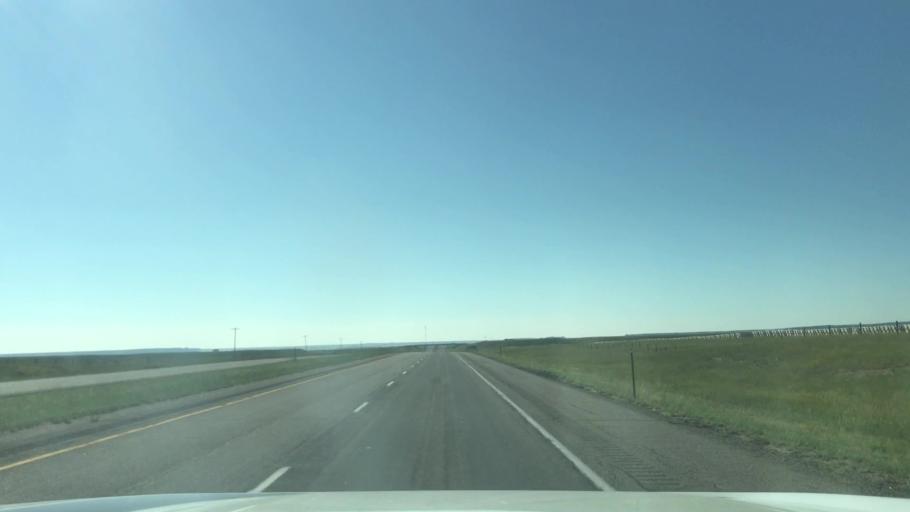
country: US
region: Wyoming
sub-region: Platte County
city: Wheatland
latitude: 41.8931
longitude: -104.8957
